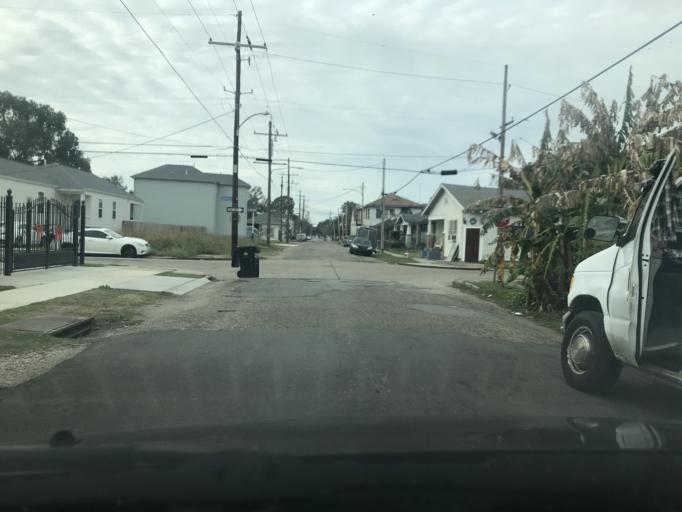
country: US
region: Louisiana
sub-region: Orleans Parish
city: New Orleans
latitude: 29.9561
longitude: -90.1108
